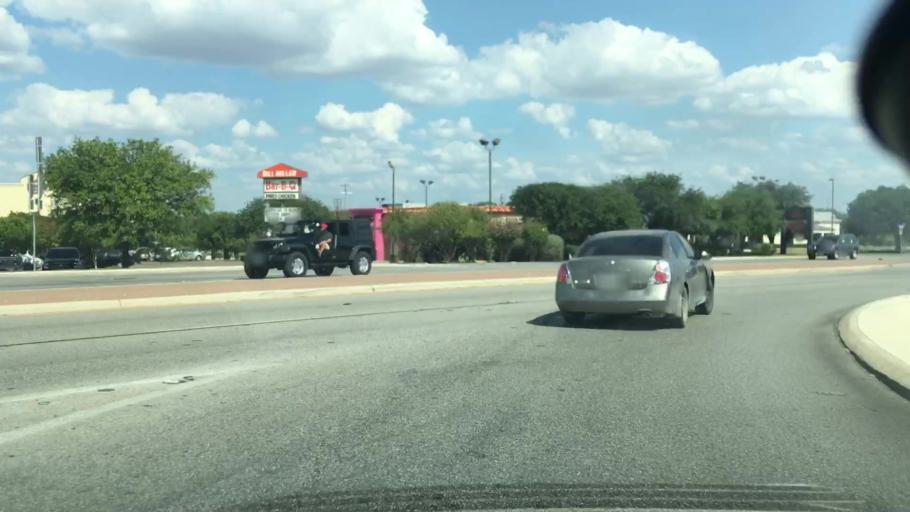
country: US
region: Texas
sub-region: Bexar County
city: Selma
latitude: 29.5993
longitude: -98.2765
